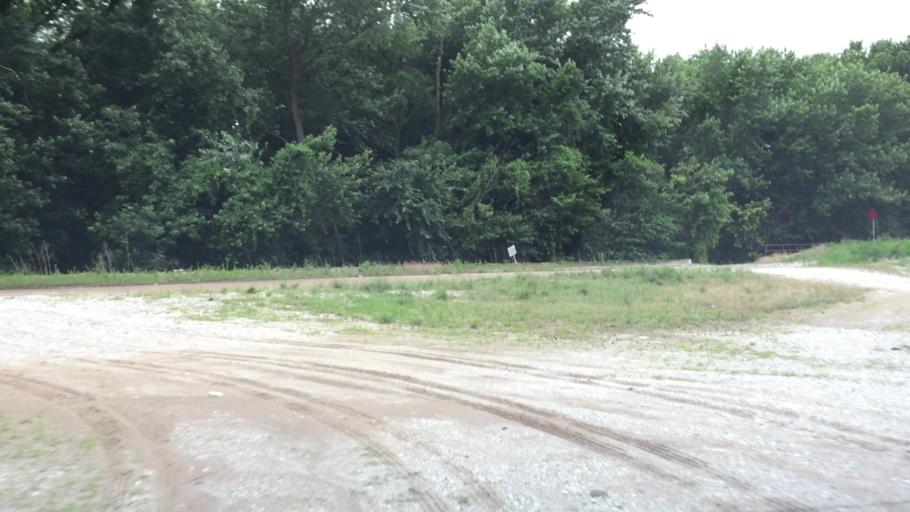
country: US
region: Iowa
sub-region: Lee County
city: Keokuk
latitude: 40.3898
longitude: -91.3665
